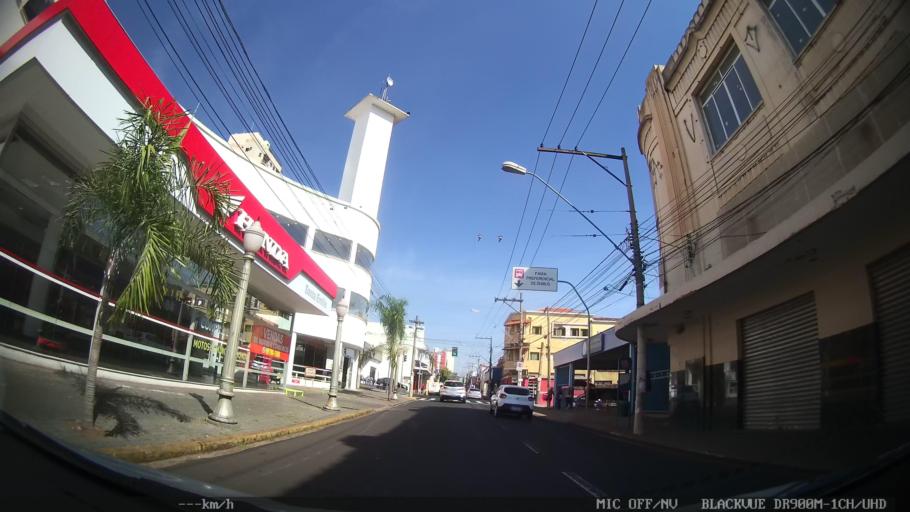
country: BR
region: Sao Paulo
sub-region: Ribeirao Preto
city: Ribeirao Preto
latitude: -21.1747
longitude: -47.8121
